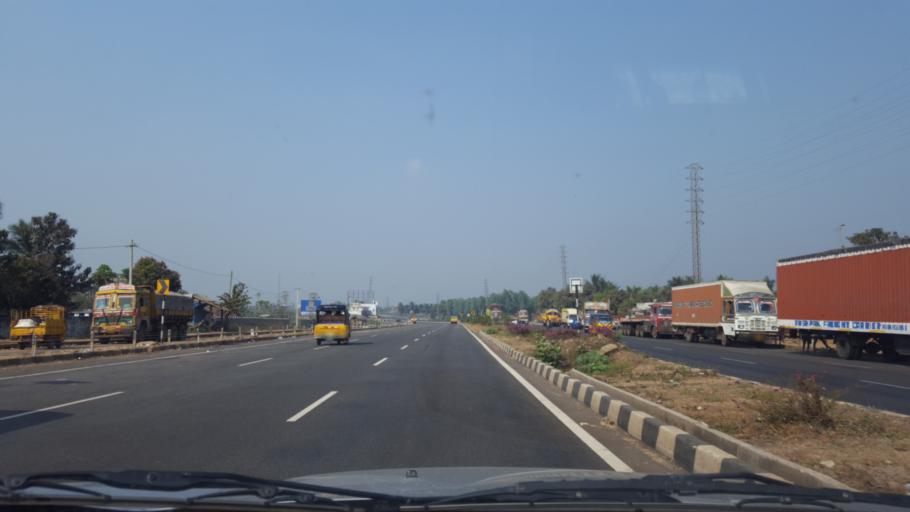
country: IN
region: Andhra Pradesh
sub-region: Vishakhapatnam
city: Bhimunipatnam
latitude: 17.9637
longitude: 83.4272
